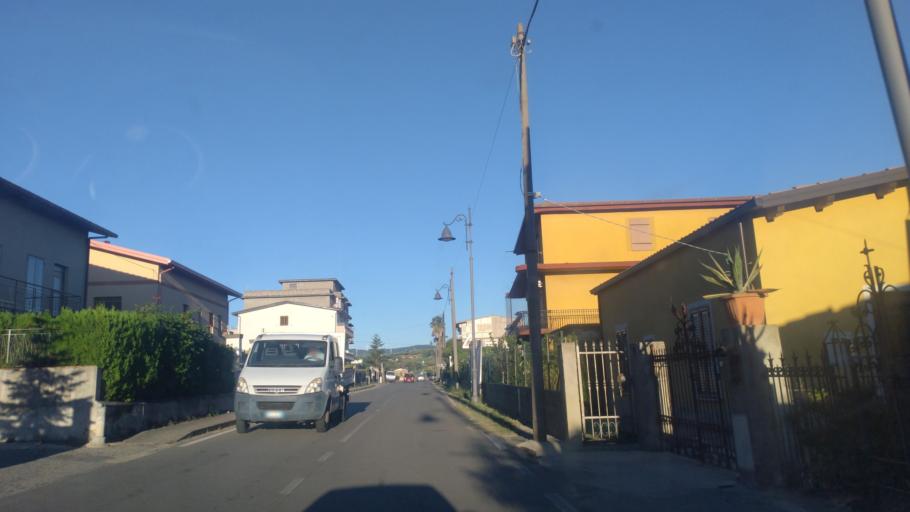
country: IT
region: Calabria
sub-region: Provincia di Catanzaro
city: Staletti
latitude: 38.7656
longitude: 16.5355
